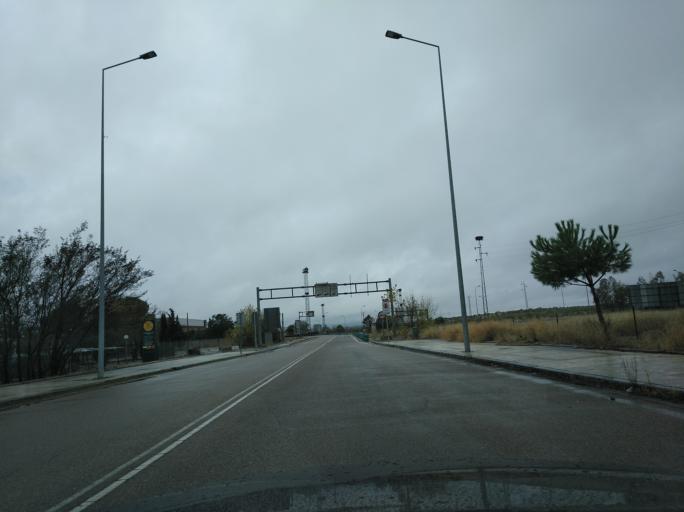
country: ES
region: Extremadura
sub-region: Provincia de Badajoz
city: Badajoz
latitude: 38.8835
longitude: -7.0282
